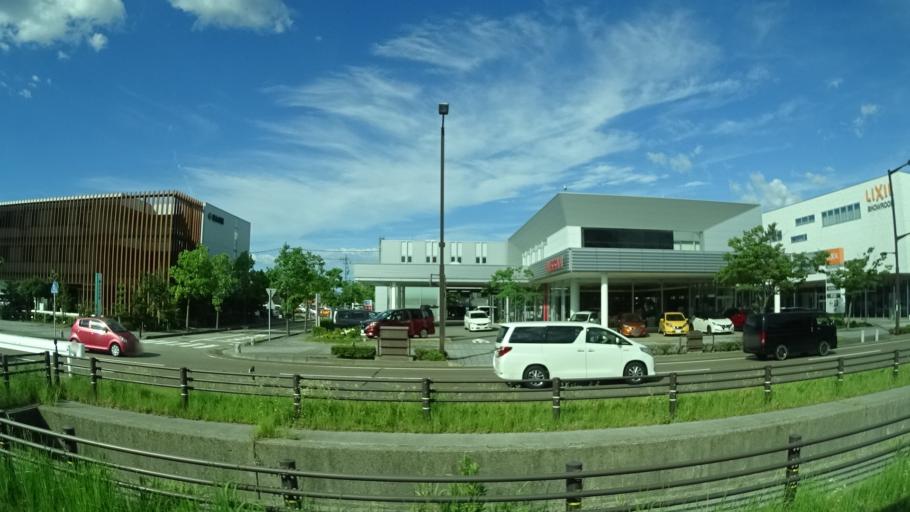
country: JP
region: Ishikawa
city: Kanazawa-shi
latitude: 36.5975
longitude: 136.6245
